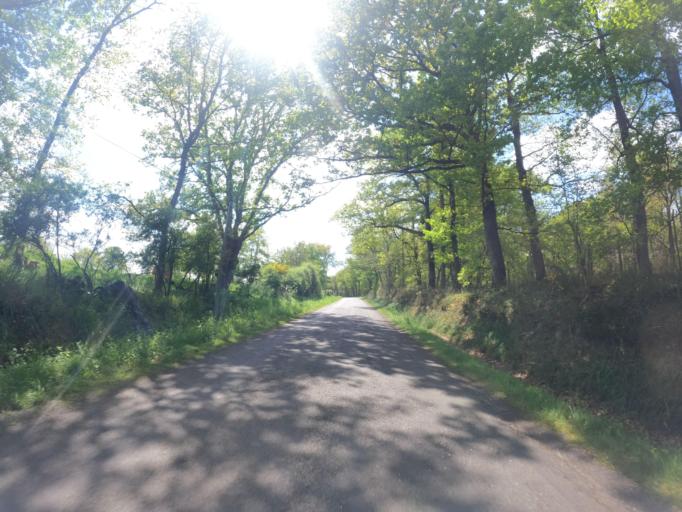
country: FR
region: Poitou-Charentes
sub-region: Departement des Deux-Sevres
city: Chiche
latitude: 46.7843
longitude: -0.3154
